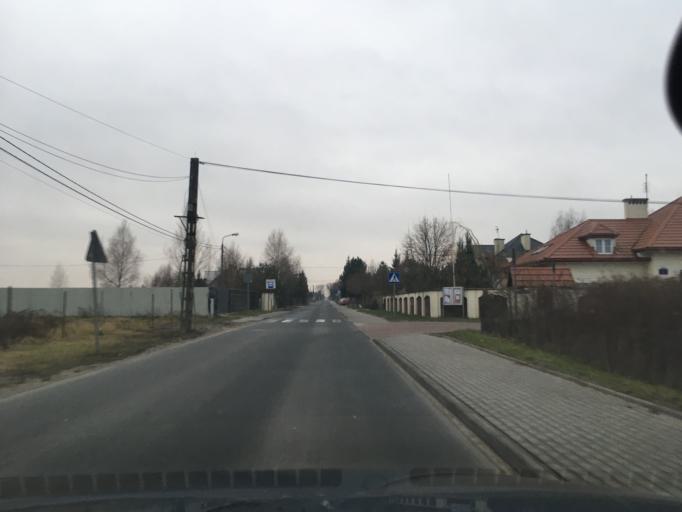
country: PL
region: Masovian Voivodeship
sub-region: Powiat piaseczynski
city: Mysiadlo
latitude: 52.1287
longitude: 20.9798
